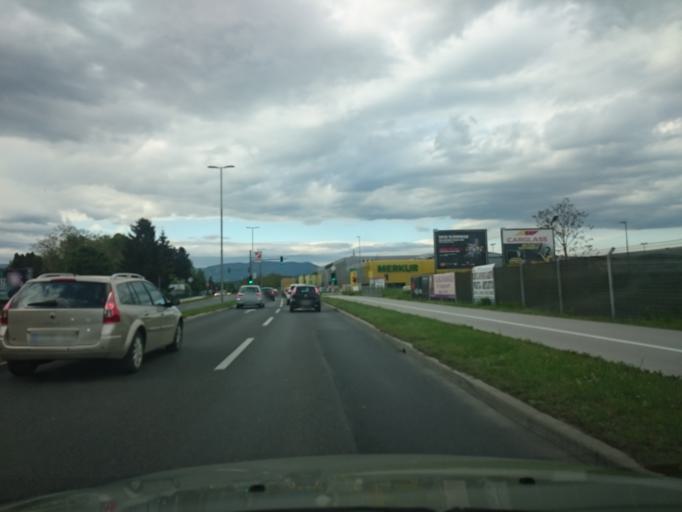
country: SI
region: Celje
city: Trnovlje pri Celju
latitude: 46.2473
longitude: 15.2796
